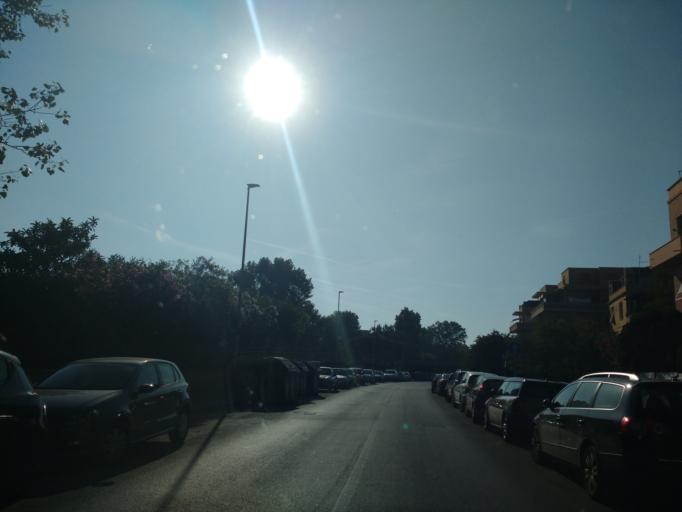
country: IT
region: Latium
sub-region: Citta metropolitana di Roma Capitale
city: Lido di Ostia
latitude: 41.7288
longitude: 12.2865
